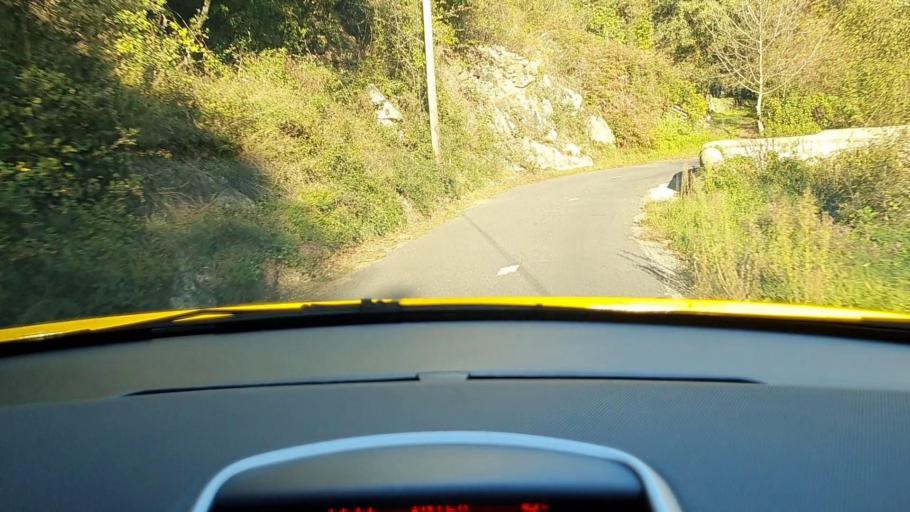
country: FR
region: Languedoc-Roussillon
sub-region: Departement du Gard
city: Sumene
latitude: 44.0273
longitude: 3.7608
